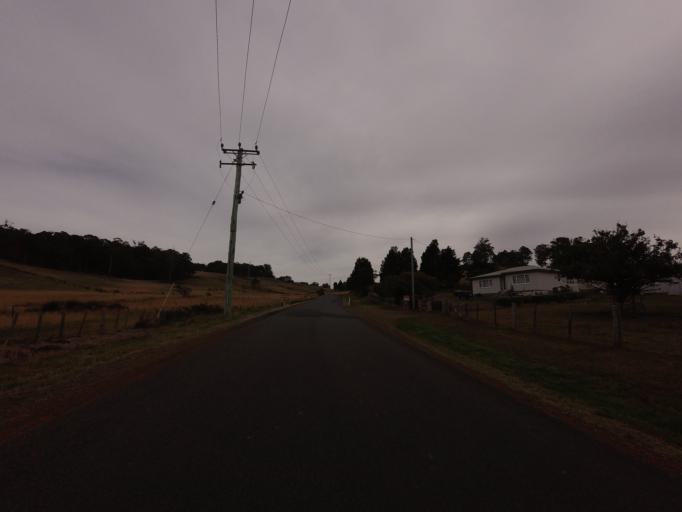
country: AU
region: Tasmania
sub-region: Sorell
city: Sorell
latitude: -42.5383
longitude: 147.5692
